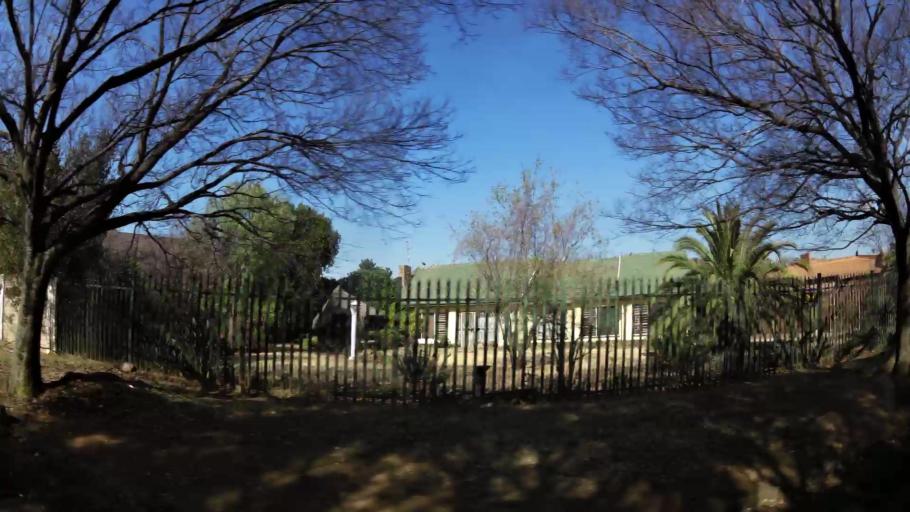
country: ZA
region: Gauteng
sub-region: West Rand District Municipality
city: Randfontein
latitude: -26.1525
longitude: 27.7044
